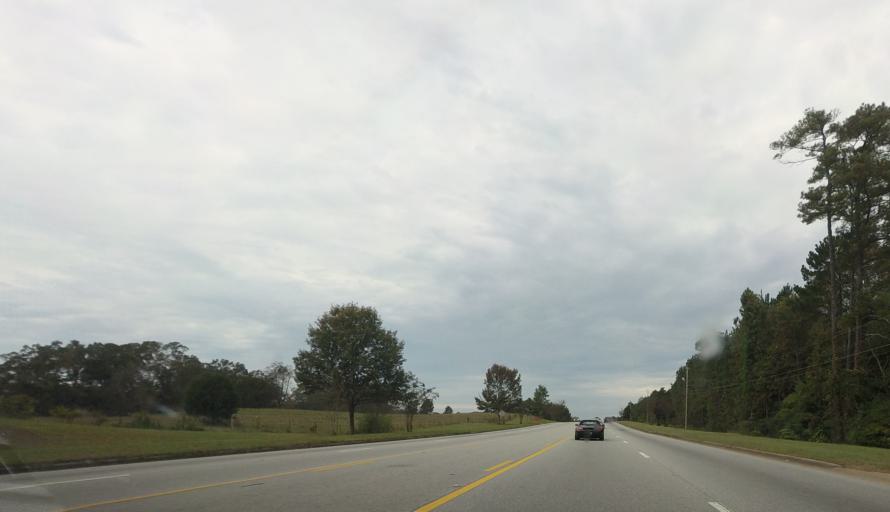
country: US
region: Alabama
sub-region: Lee County
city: Opelika
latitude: 32.6420
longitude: -85.3299
